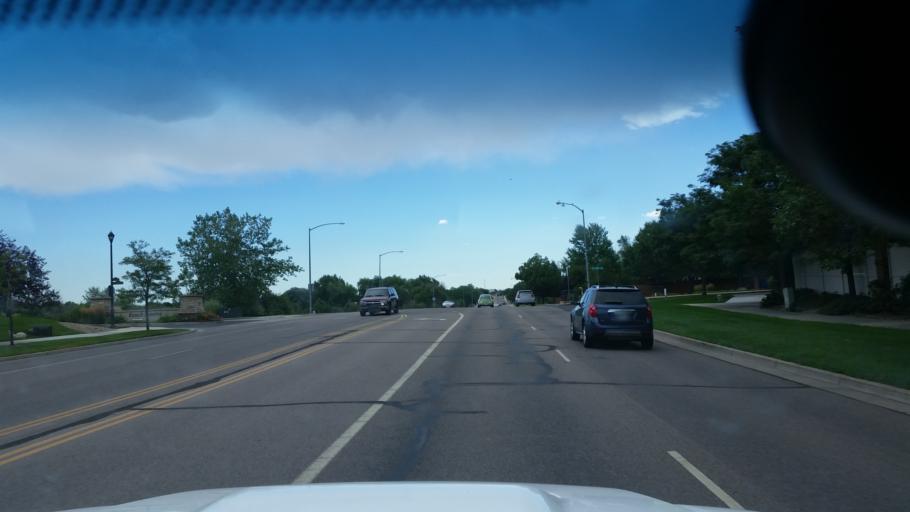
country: US
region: Colorado
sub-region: Adams County
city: Northglenn
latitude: 39.8996
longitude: -105.0210
